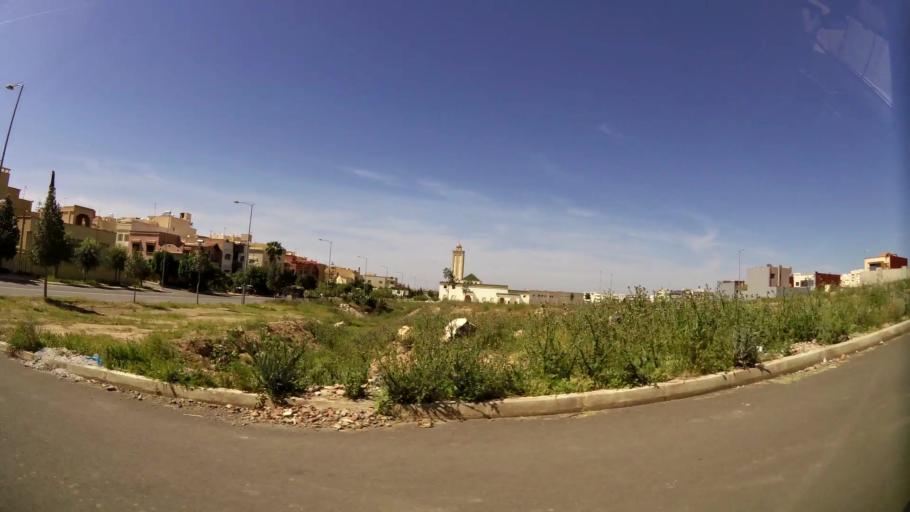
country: MA
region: Oriental
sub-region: Oujda-Angad
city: Oujda
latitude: 34.6518
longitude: -1.9132
